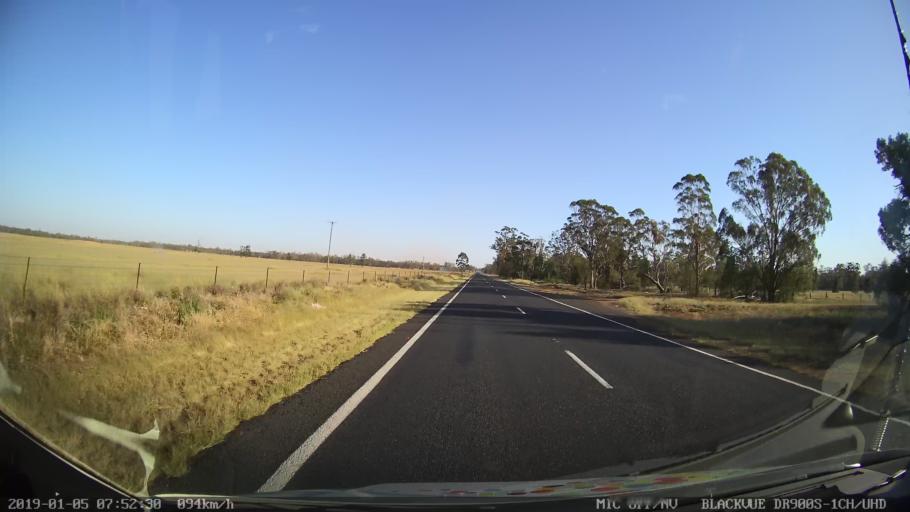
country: AU
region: New South Wales
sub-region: Gilgandra
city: Gilgandra
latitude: -31.7575
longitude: 148.6403
